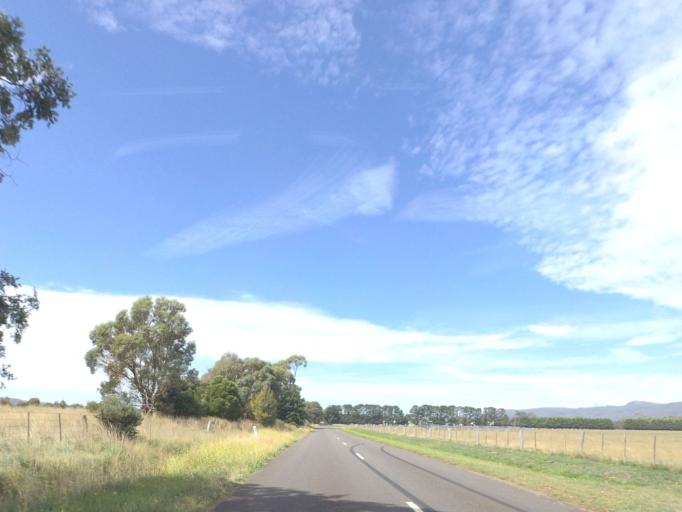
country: AU
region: Victoria
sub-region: Hume
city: Sunbury
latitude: -37.3218
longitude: 144.5293
